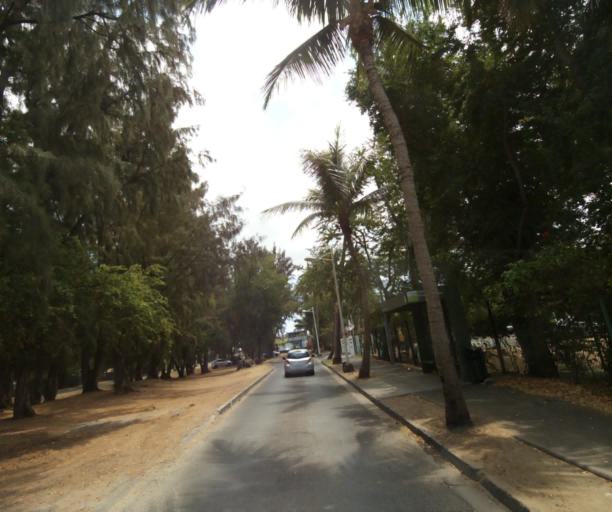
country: RE
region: Reunion
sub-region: Reunion
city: Saint-Paul
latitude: -21.0693
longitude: 55.2230
